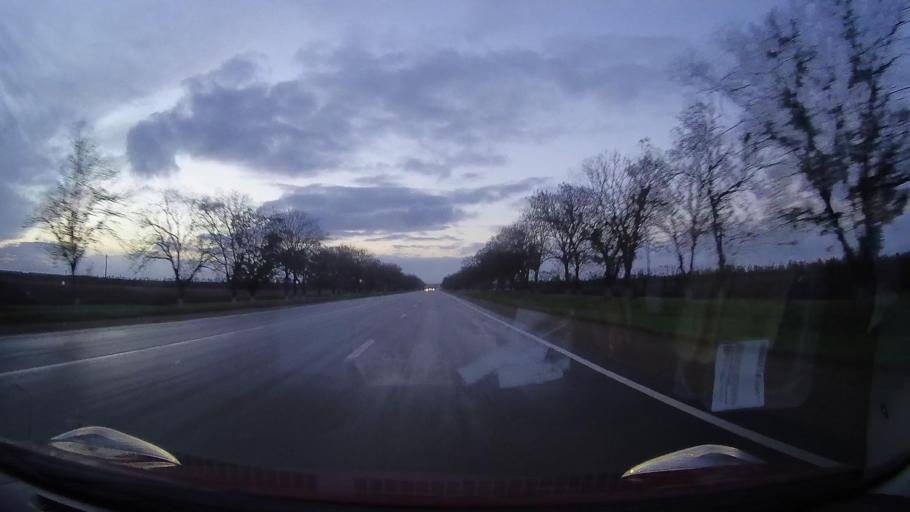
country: RU
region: Krasnodarskiy
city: Zavetnyy
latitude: 44.9019
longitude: 41.1826
